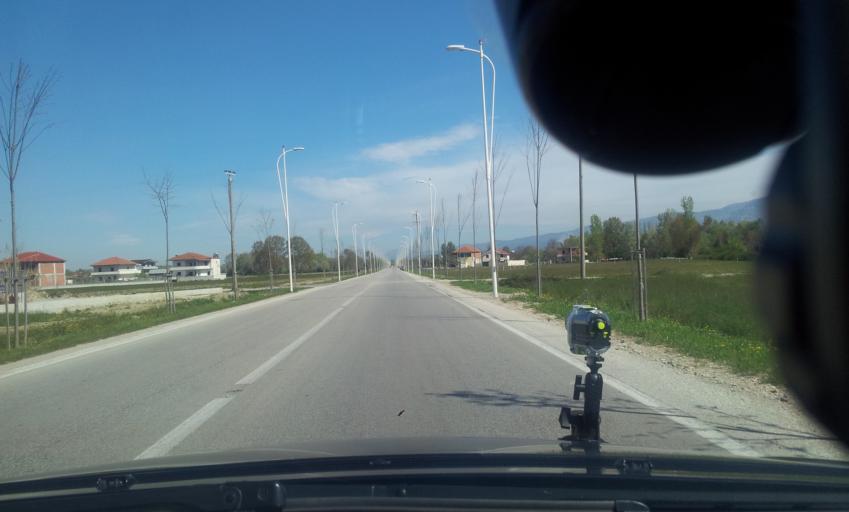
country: AL
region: Tirane
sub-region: Rrethi i Tiranes
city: Berxull
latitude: 41.3868
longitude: 19.7034
